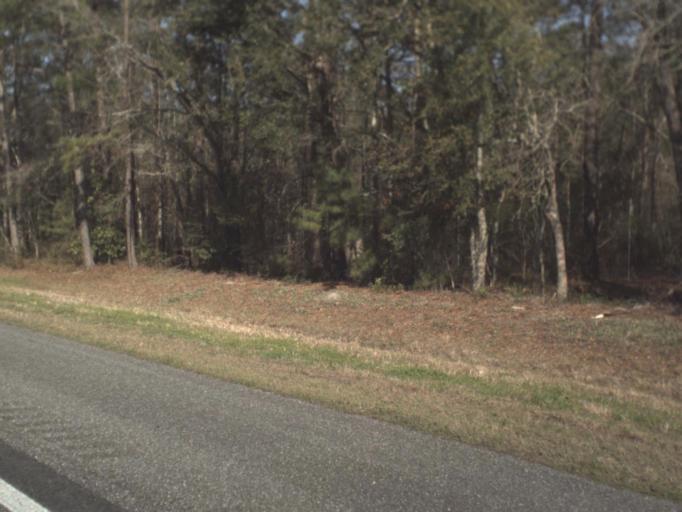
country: US
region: Florida
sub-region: Jefferson County
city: Monticello
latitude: 30.4727
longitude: -83.8293
